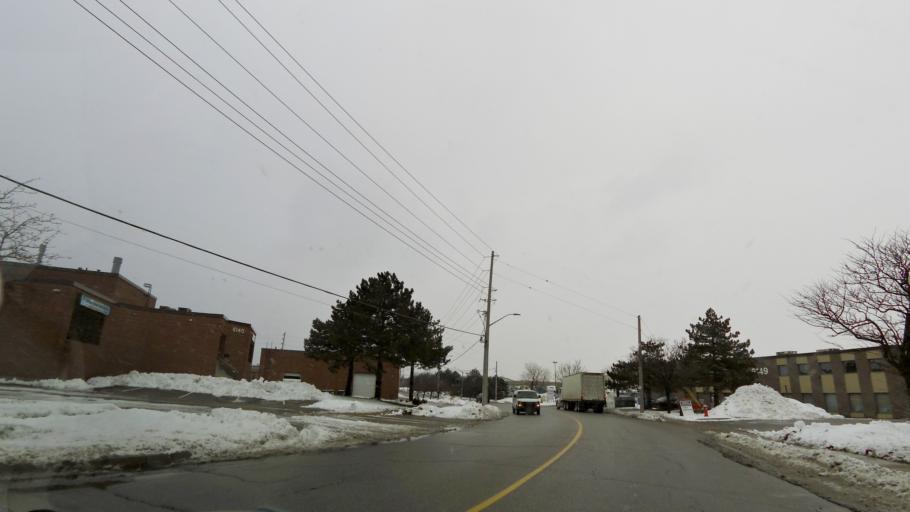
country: CA
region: Ontario
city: Mississauga
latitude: 43.6512
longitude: -79.6577
